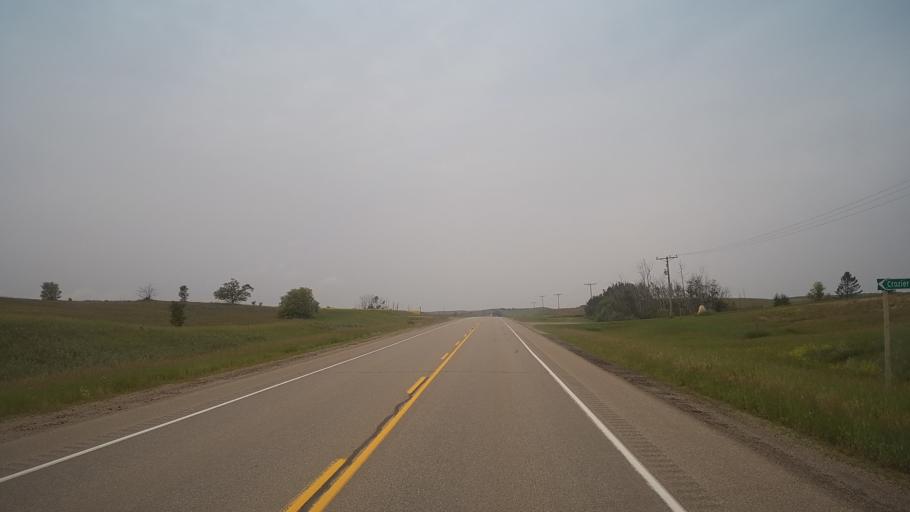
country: CA
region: Saskatchewan
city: Biggar
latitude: 52.0565
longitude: -107.8569
